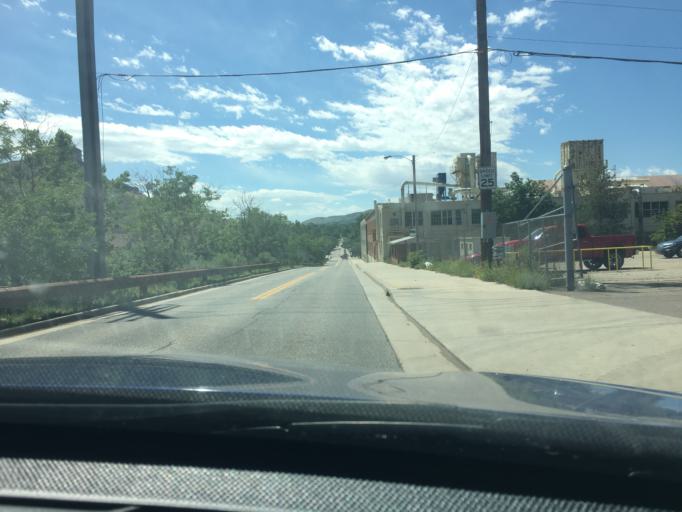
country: US
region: Colorado
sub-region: Jefferson County
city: Golden
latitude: 39.7609
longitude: -105.2233
